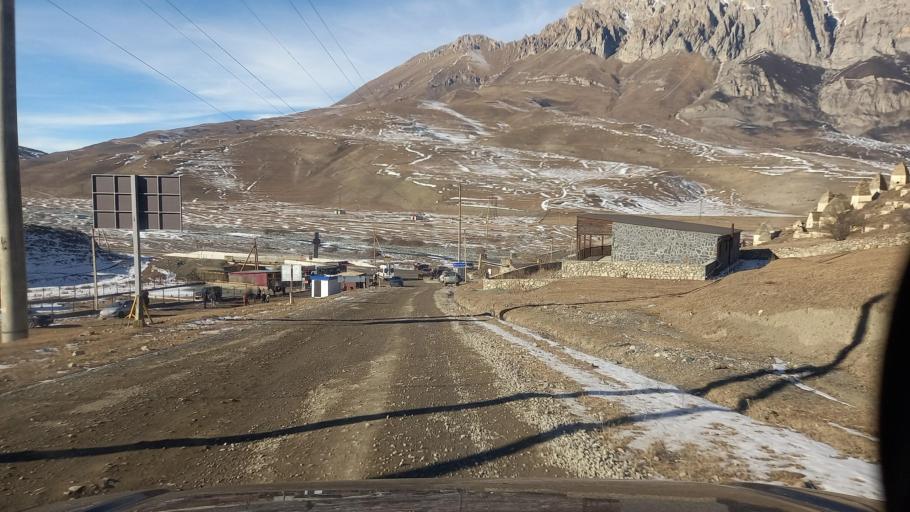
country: RU
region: North Ossetia
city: Verkhniy Fiagdon
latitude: 42.8399
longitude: 44.4466
